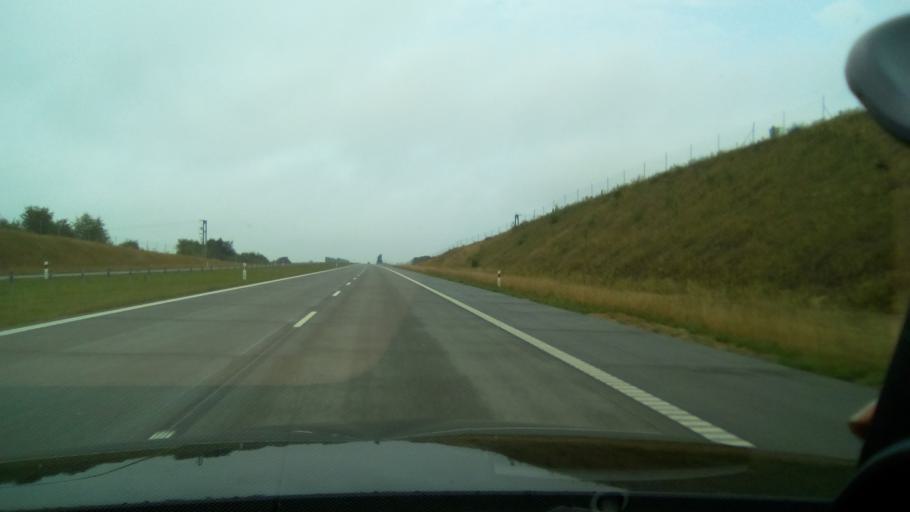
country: PL
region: Silesian Voivodeship
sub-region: Powiat klobucki
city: Kalej
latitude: 50.8301
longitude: 19.0275
